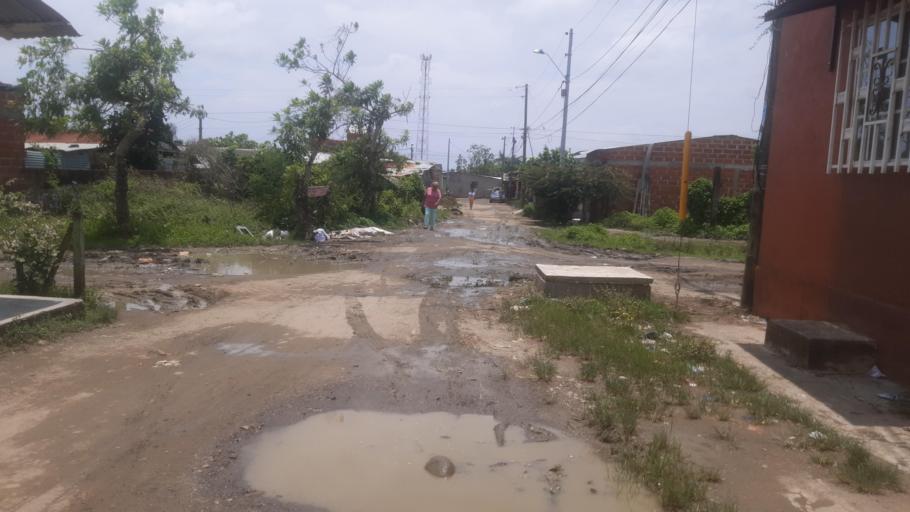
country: CO
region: Antioquia
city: Apartado
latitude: 8.0007
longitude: -76.6297
